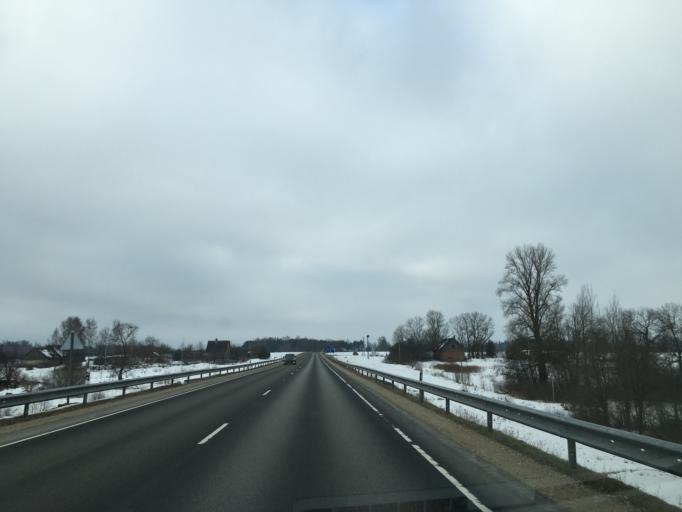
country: EE
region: Tartu
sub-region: Elva linn
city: Elva
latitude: 58.1939
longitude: 26.3517
